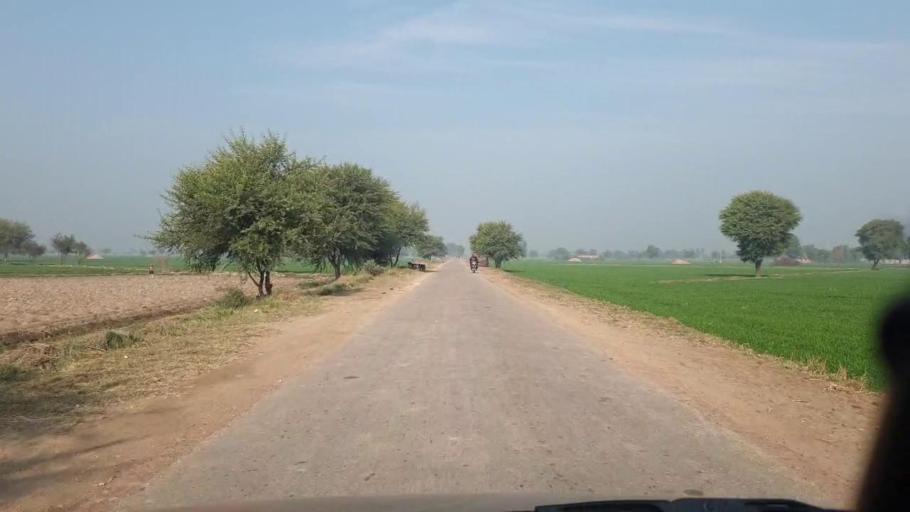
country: PK
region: Sindh
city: Shahdadpur
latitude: 26.0029
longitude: 68.5542
